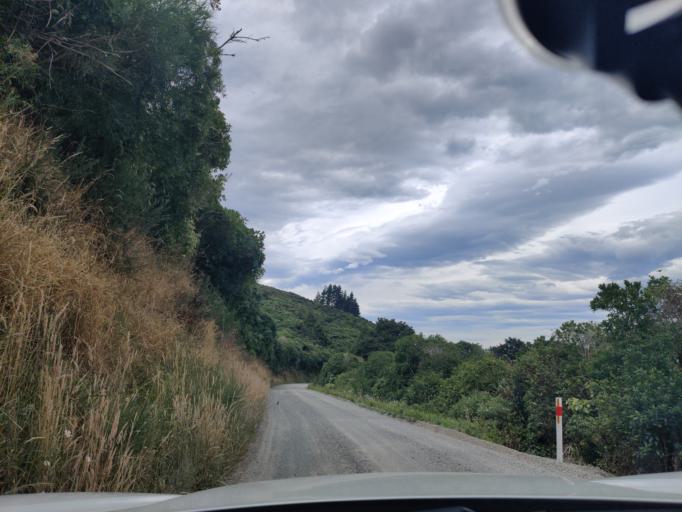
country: NZ
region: Wellington
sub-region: Masterton District
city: Masterton
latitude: -41.0402
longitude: 175.4108
